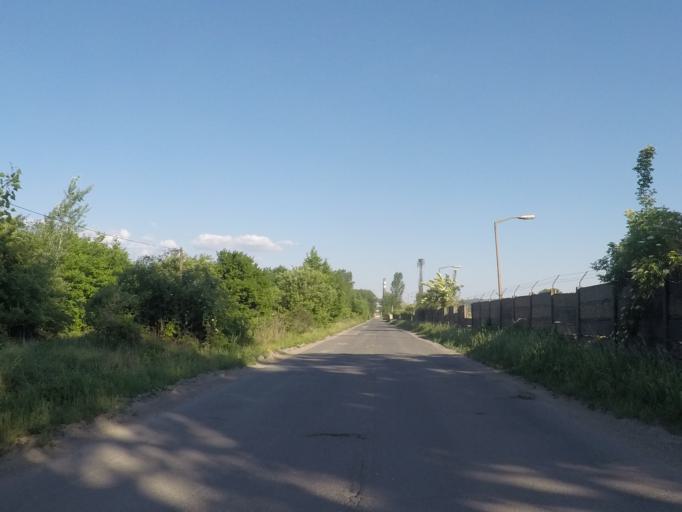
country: HU
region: Borsod-Abauj-Zemplen
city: Mucsony
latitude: 48.2449
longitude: 20.6690
